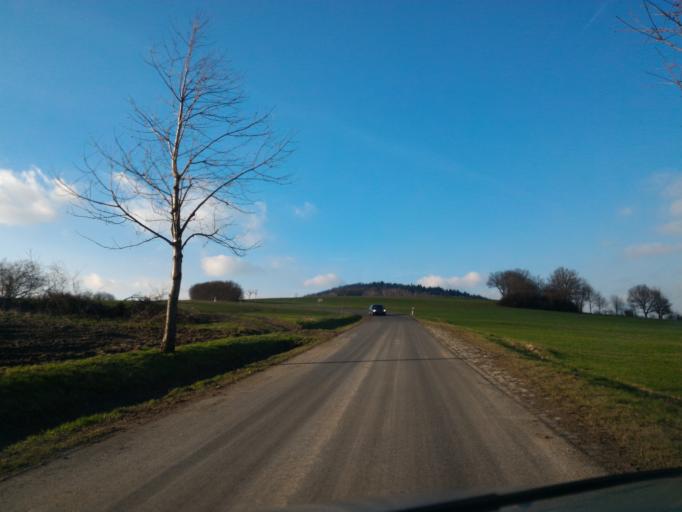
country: DE
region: Saxony
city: Kurort Jonsdorf
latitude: 50.8809
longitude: 14.7070
